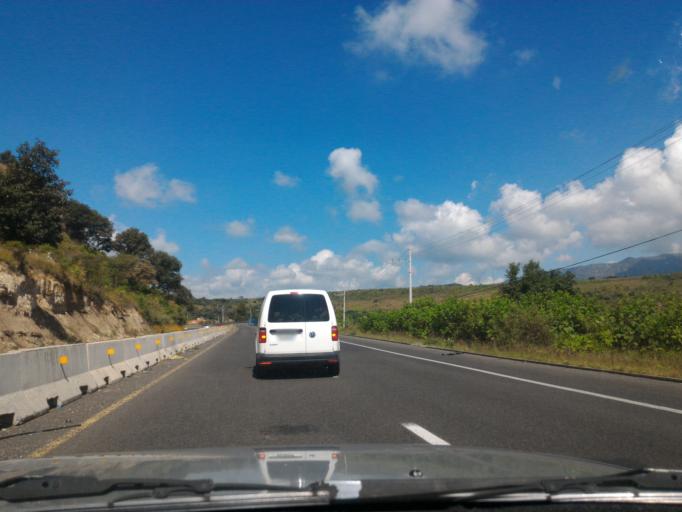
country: MX
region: Jalisco
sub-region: Tala
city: Los Ruisenores
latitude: 20.7383
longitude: -103.6263
